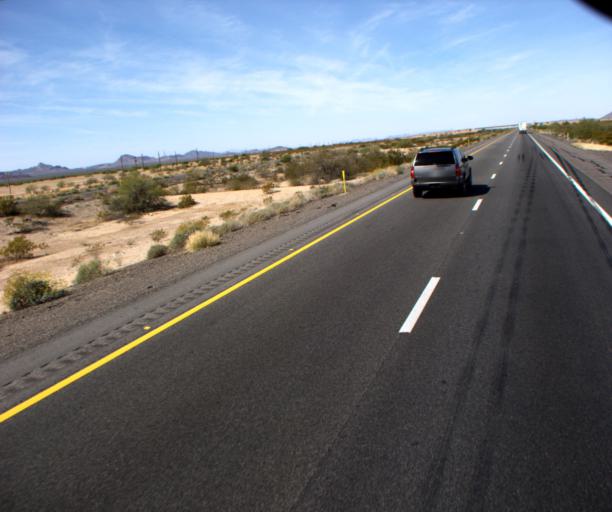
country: US
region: Arizona
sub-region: La Paz County
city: Salome
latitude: 33.5674
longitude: -113.3402
